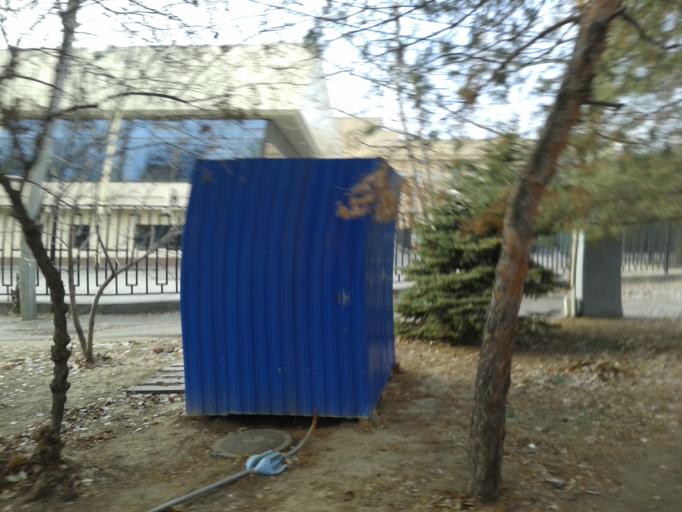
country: RU
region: Volgograd
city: Volgograd
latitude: 48.7090
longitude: 44.5065
